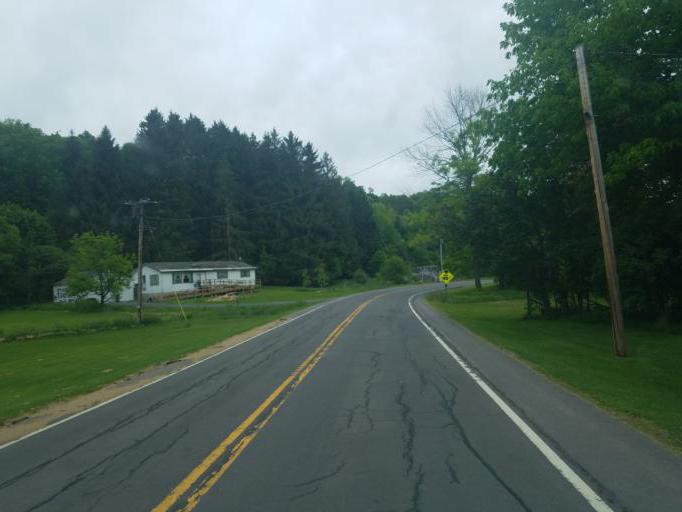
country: US
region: New York
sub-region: Herkimer County
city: Frankfort
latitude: 42.9710
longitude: -75.1004
